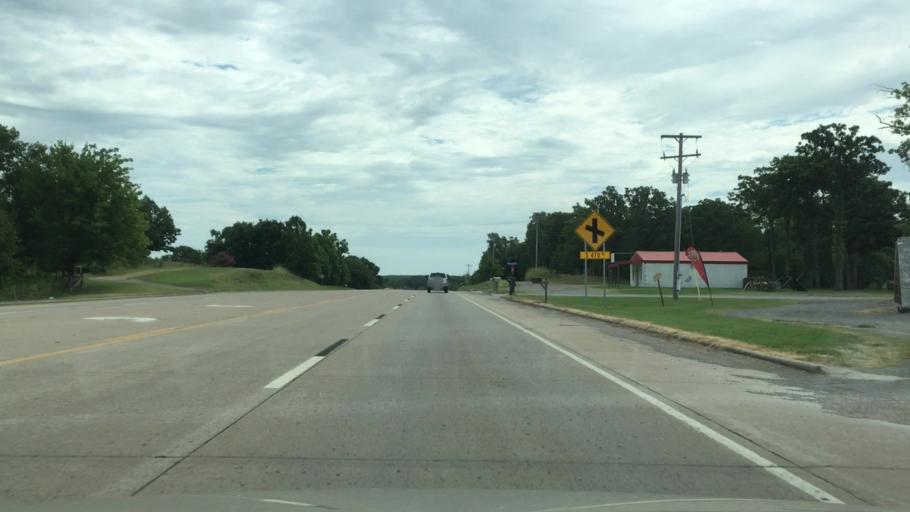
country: US
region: Oklahoma
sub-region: Cherokee County
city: Park Hill
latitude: 35.8162
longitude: -95.0597
